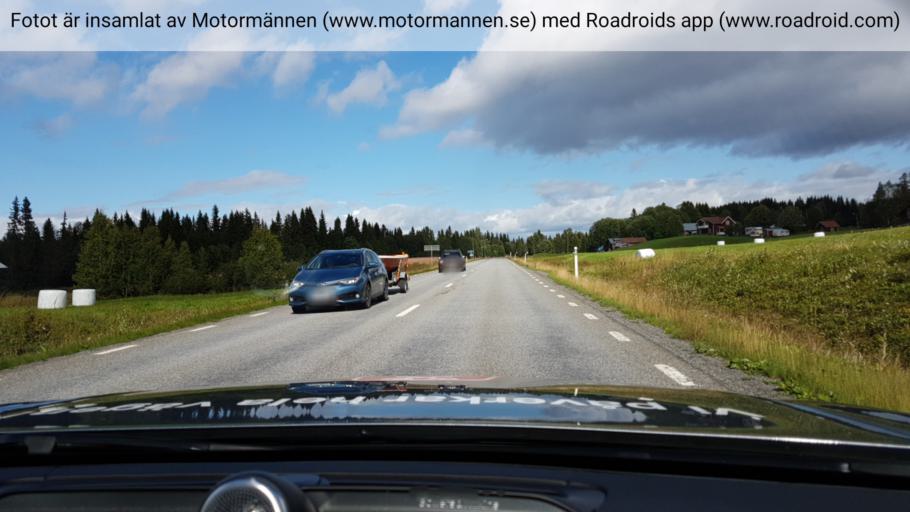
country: SE
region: Jaemtland
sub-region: OEstersunds Kommun
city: Lit
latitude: 63.4321
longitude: 15.1215
